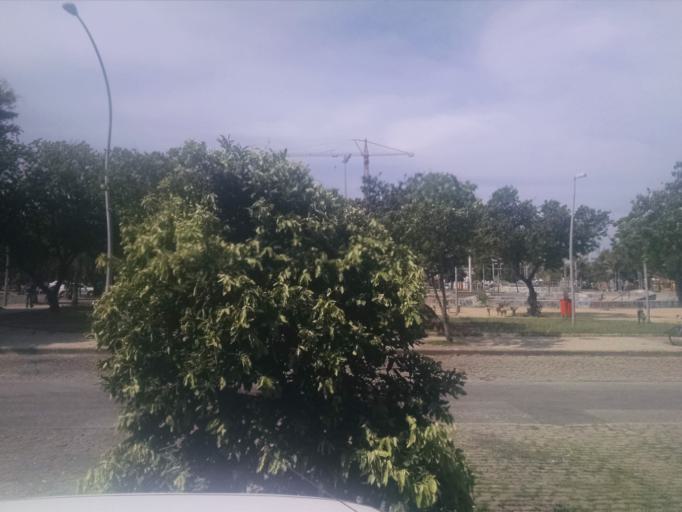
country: BR
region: Rio de Janeiro
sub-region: Rio De Janeiro
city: Rio de Janeiro
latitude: -23.0121
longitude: -43.3185
